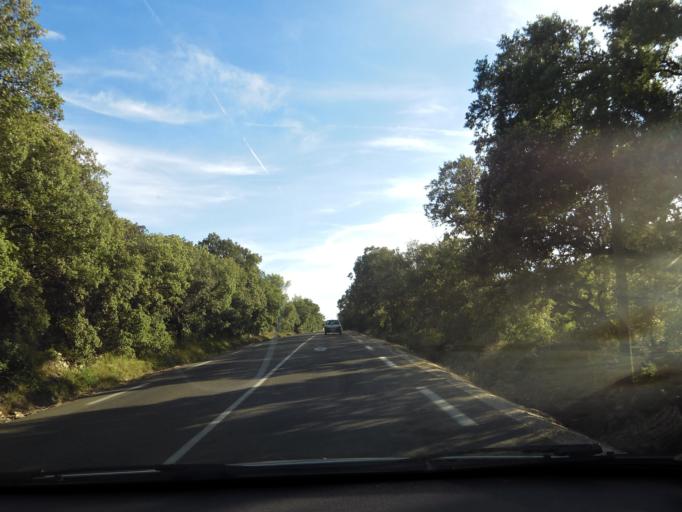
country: FR
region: Languedoc-Roussillon
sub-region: Departement de l'Herault
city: Claret
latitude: 43.8473
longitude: 3.9223
